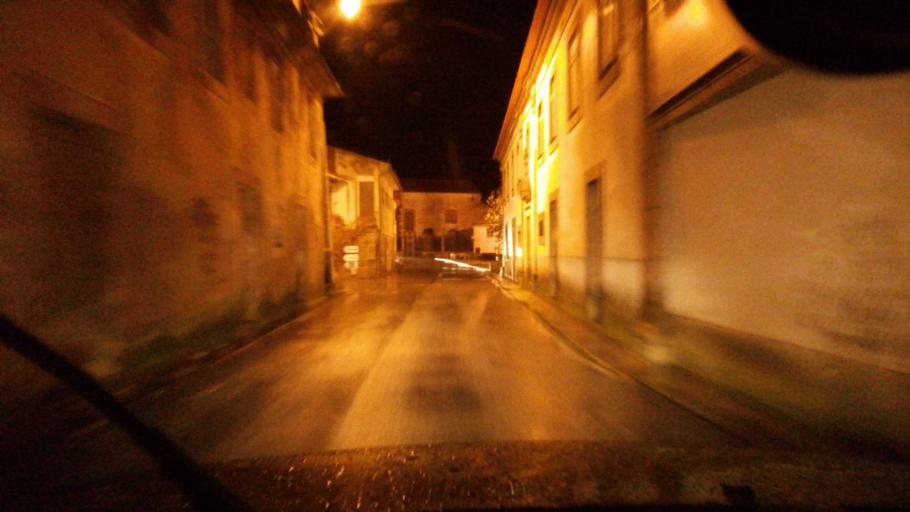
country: PT
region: Viseu
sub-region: Armamar
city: Armamar
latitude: 41.1117
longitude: -7.7179
